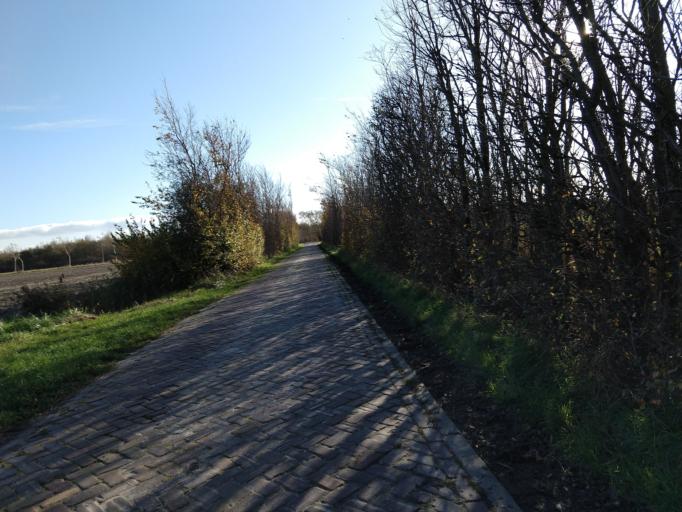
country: NL
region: Zeeland
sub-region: Gemeente Vlissingen
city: Vlissingen
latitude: 51.5087
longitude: 3.4851
